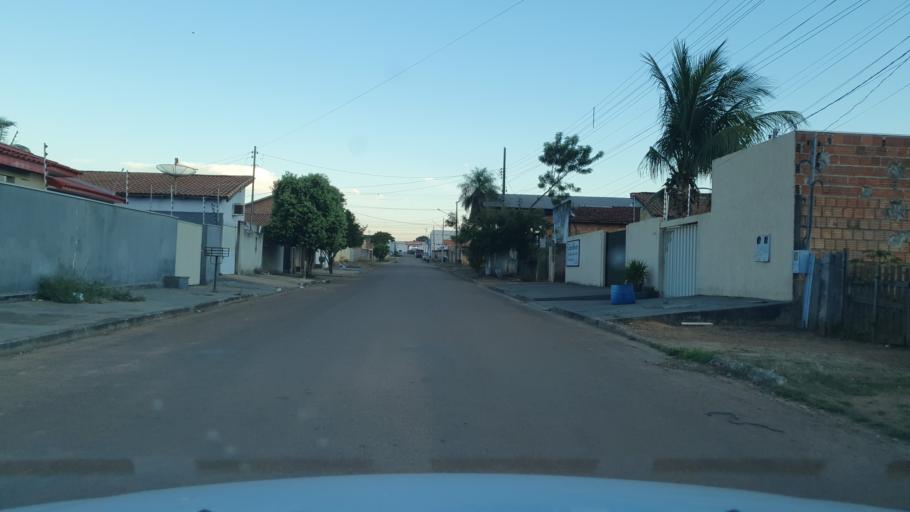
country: BR
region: Mato Grosso
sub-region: Pontes E Lacerda
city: Pontes e Lacerda
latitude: -15.2231
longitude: -59.3229
